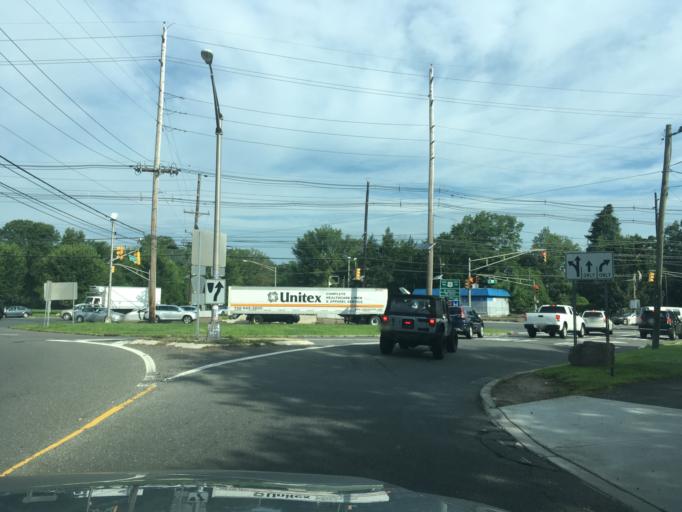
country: US
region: New Jersey
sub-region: Mercer County
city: Princeton Junction
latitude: 40.3311
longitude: -74.6375
